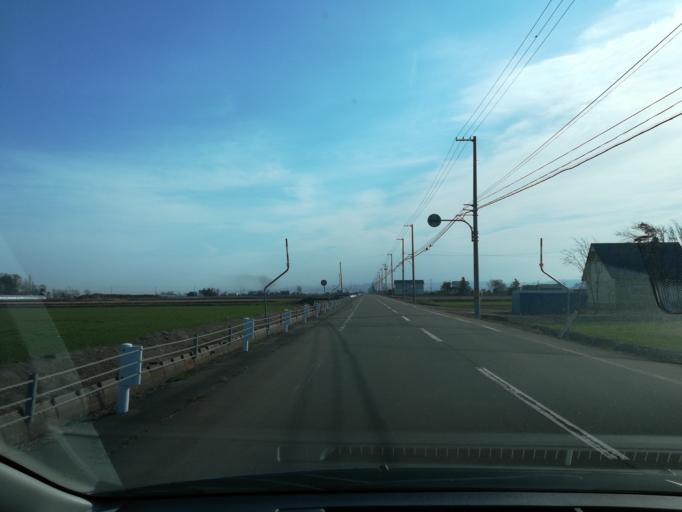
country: JP
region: Hokkaido
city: Iwamizawa
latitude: 43.1721
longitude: 141.6714
